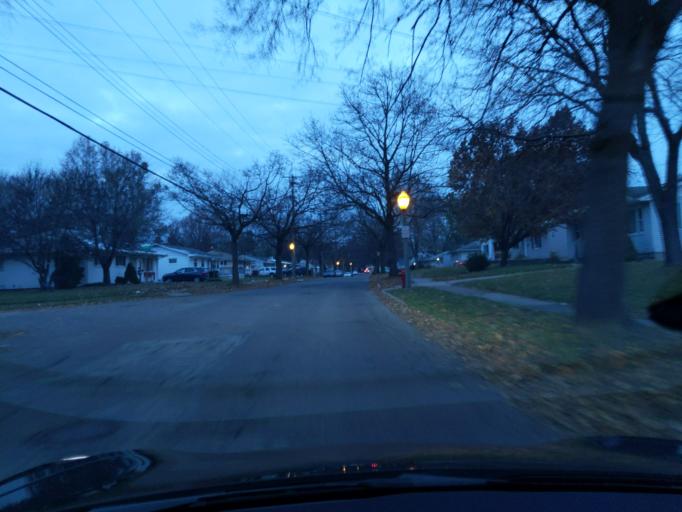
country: US
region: Michigan
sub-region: Ingham County
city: Lansing
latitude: 42.6951
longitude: -84.5584
